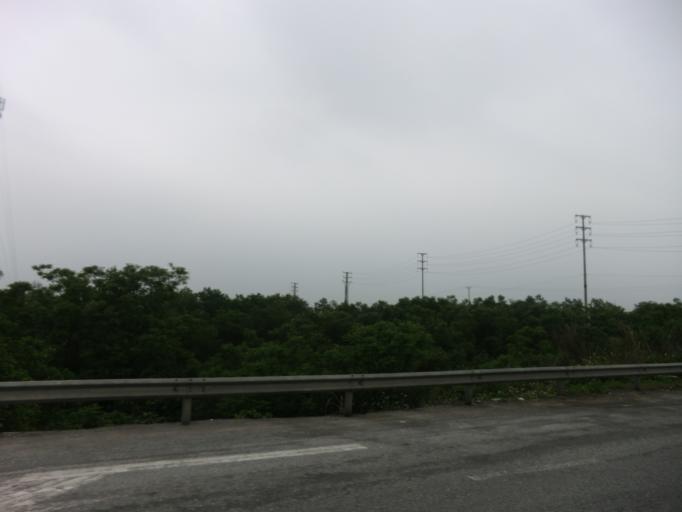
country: VN
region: Ha Tinh
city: Ky Anh
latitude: 18.0271
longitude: 106.3488
